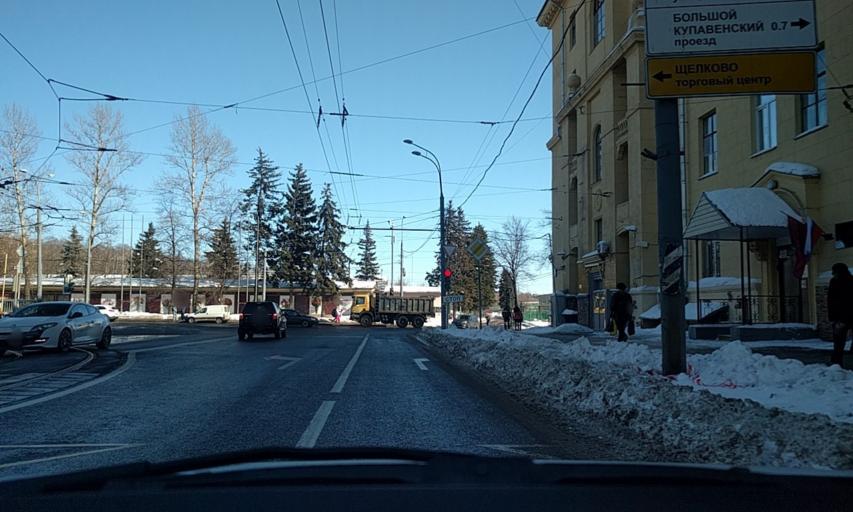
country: RU
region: Moskovskaya
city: Izmaylovo
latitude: 55.7936
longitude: 37.8226
